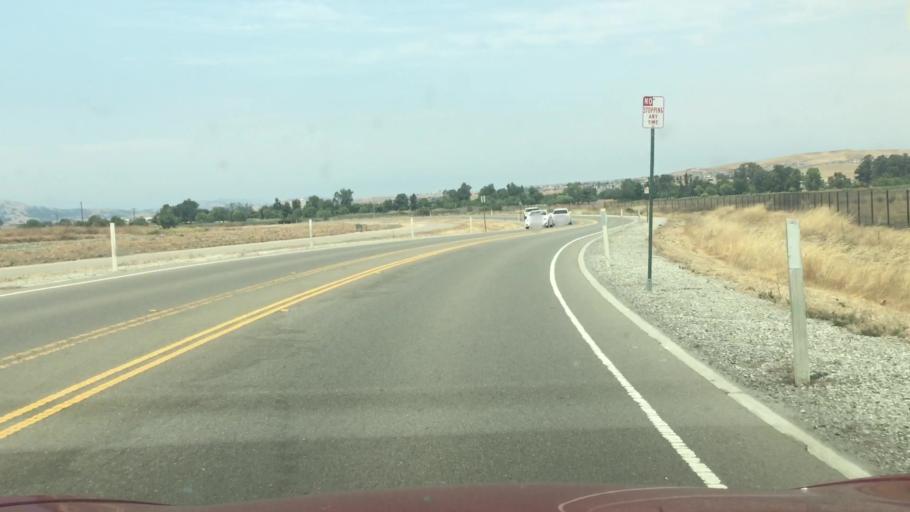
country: US
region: California
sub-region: Alameda County
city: Pleasanton
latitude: 37.6902
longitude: -121.8280
